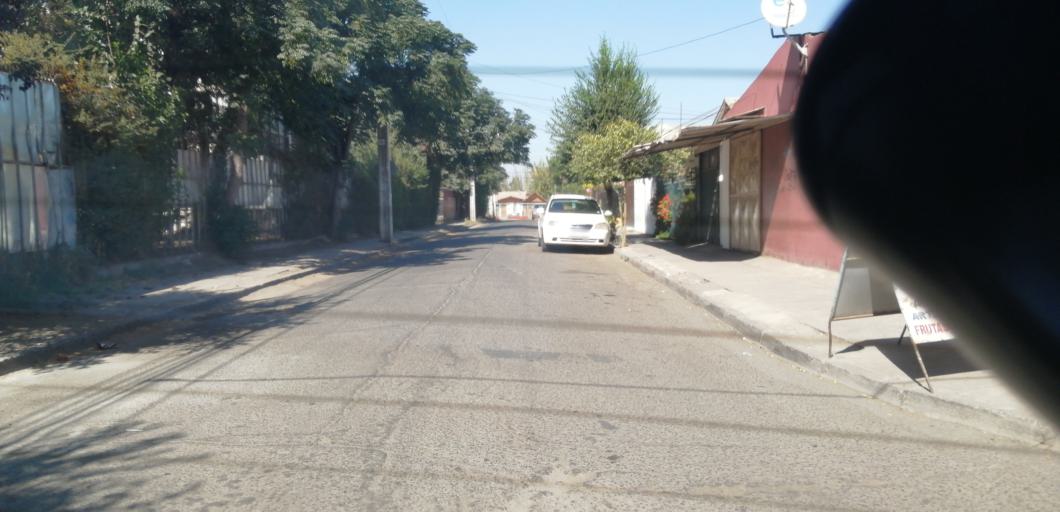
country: CL
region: Santiago Metropolitan
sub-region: Provincia de Santiago
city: Lo Prado
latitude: -33.4650
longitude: -70.7388
